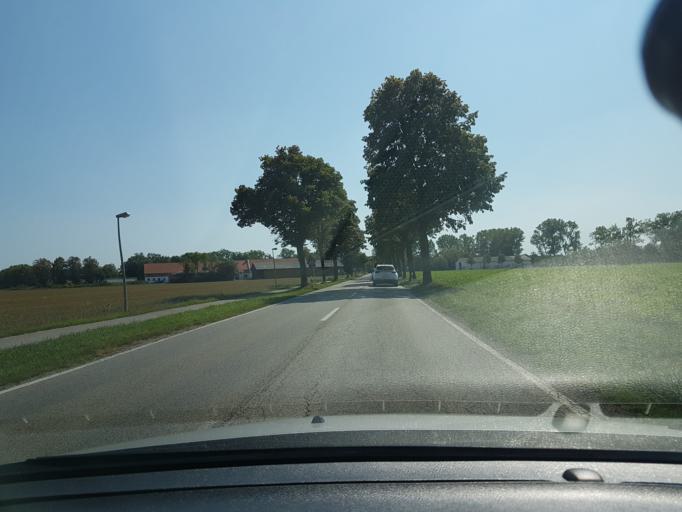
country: DE
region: Bavaria
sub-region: Upper Bavaria
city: Oberschleissheim
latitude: 48.2689
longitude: 11.5591
